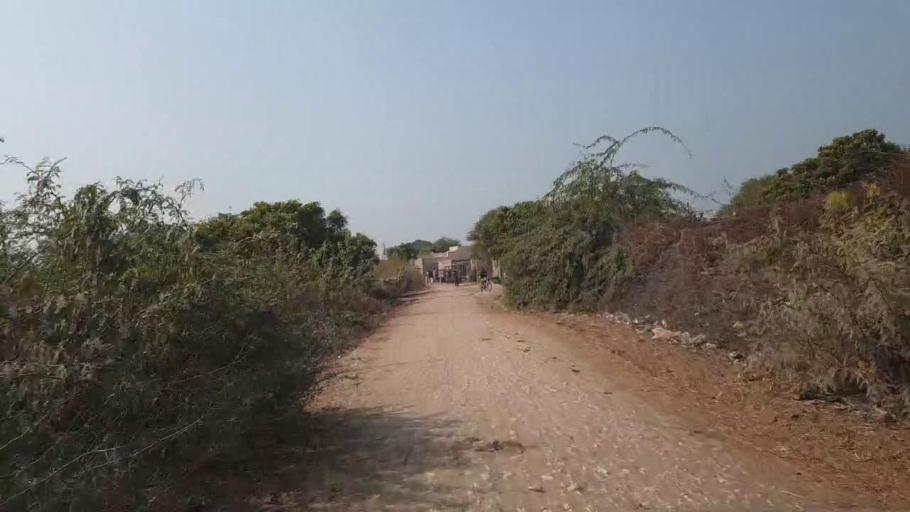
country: PK
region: Sindh
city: Bhit Shah
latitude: 25.8302
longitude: 68.4901
